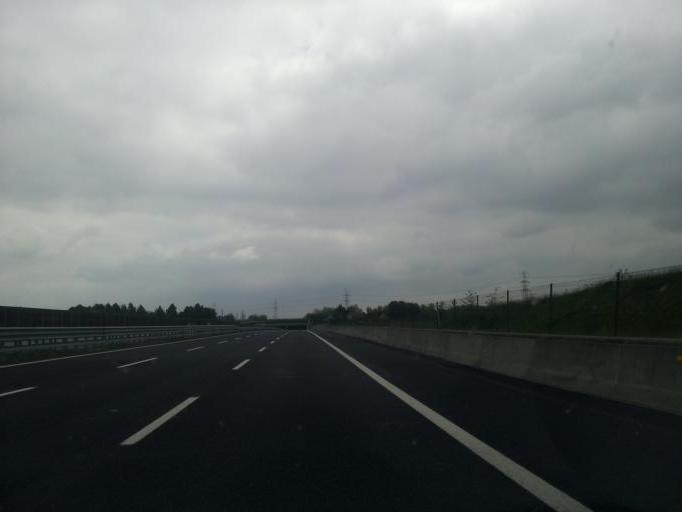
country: IT
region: Veneto
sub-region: Provincia di Treviso
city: Sambughe
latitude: 45.5883
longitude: 12.2219
